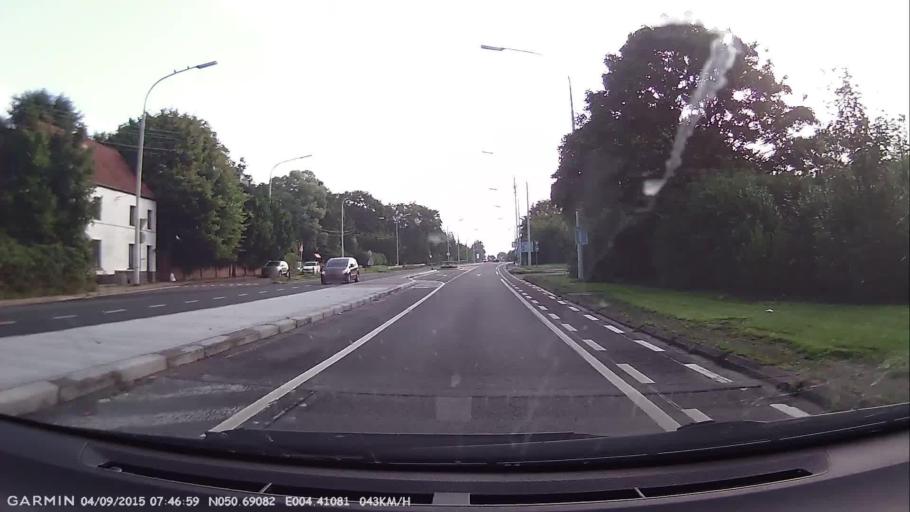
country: BE
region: Wallonia
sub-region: Province du Brabant Wallon
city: Waterloo
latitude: 50.6909
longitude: 4.4111
